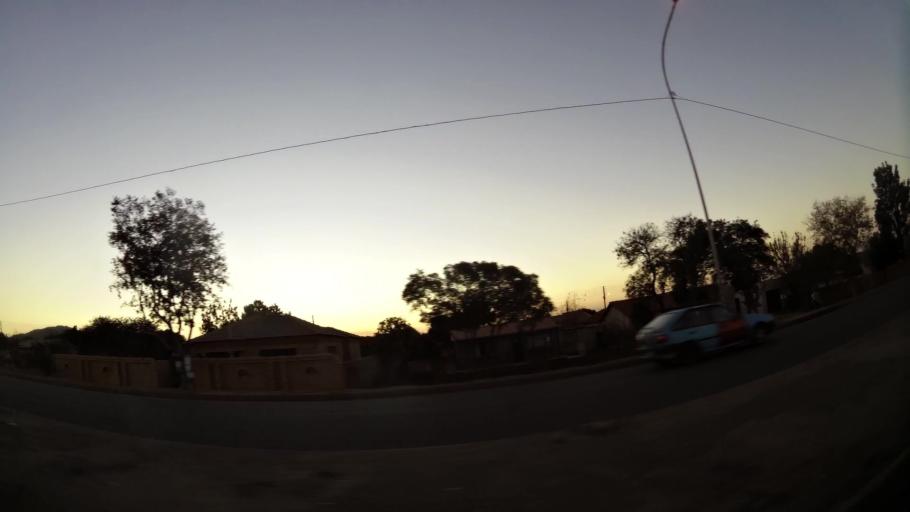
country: ZA
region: North-West
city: Ga-Rankuwa
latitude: -25.6000
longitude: 27.9743
